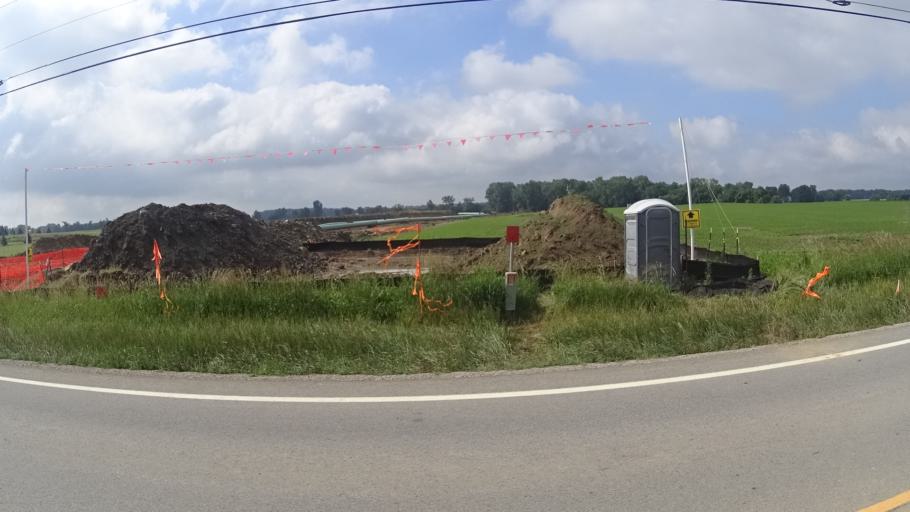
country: US
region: Ohio
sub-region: Huron County
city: Wakeman
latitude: 41.3073
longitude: -82.4590
